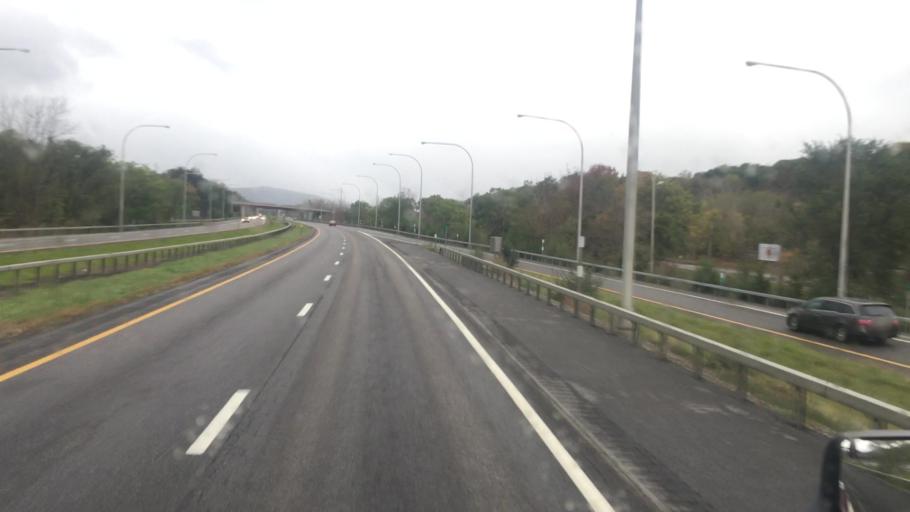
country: US
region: New York
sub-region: Broome County
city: Endwell
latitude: 42.1137
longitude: -76.0028
